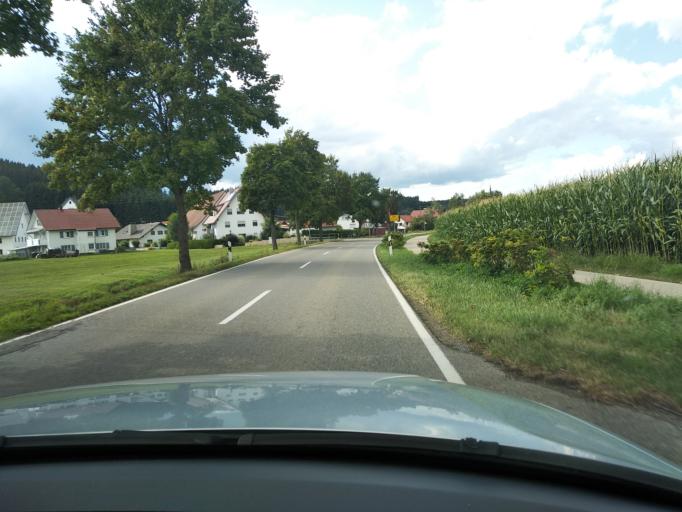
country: DE
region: Bavaria
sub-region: Swabia
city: Woringen
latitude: 47.8957
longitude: 10.2086
